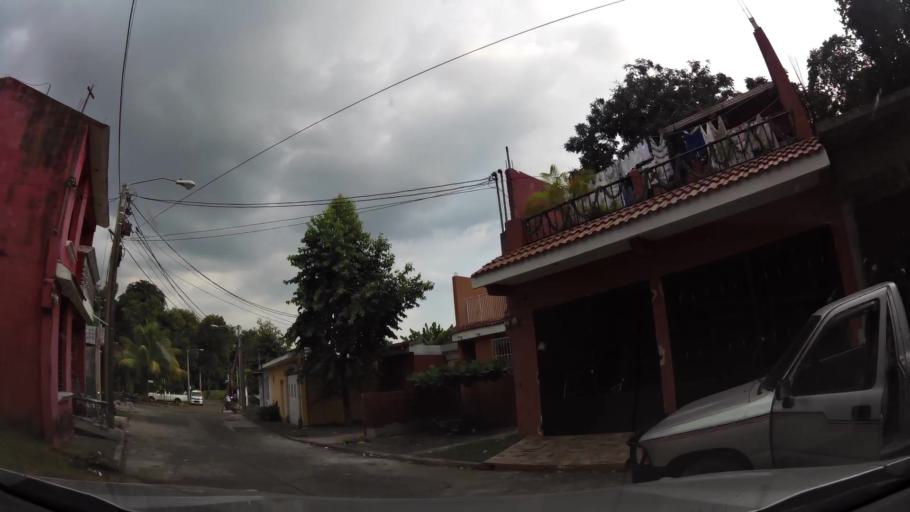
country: GT
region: Escuintla
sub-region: Municipio de Escuintla
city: Escuintla
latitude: 14.3086
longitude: -90.7775
